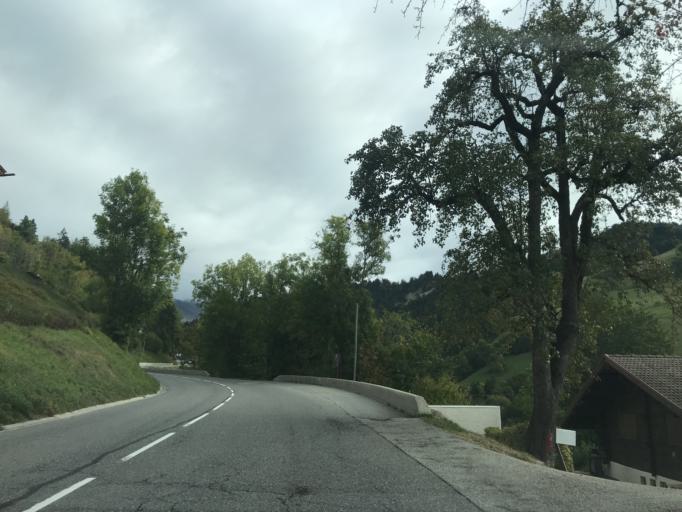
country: FR
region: Rhone-Alpes
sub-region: Departement de la Haute-Savoie
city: Le Grand-Bornand
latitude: 45.9486
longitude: 6.4345
